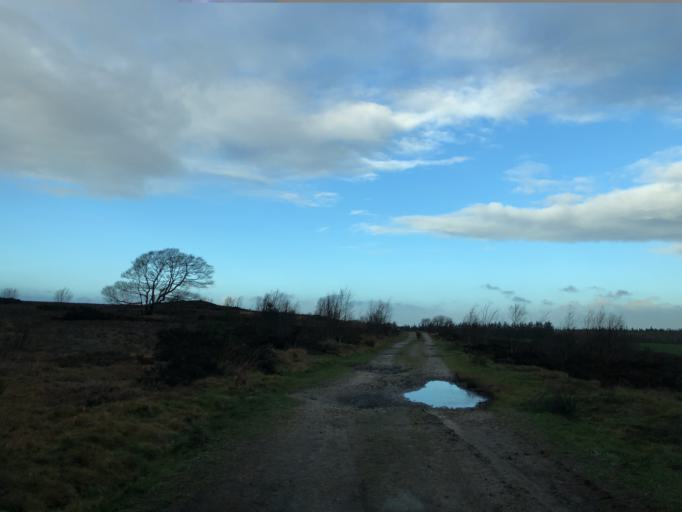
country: DK
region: Central Jutland
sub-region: Ringkobing-Skjern Kommune
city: Videbaek
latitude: 56.1848
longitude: 8.6613
